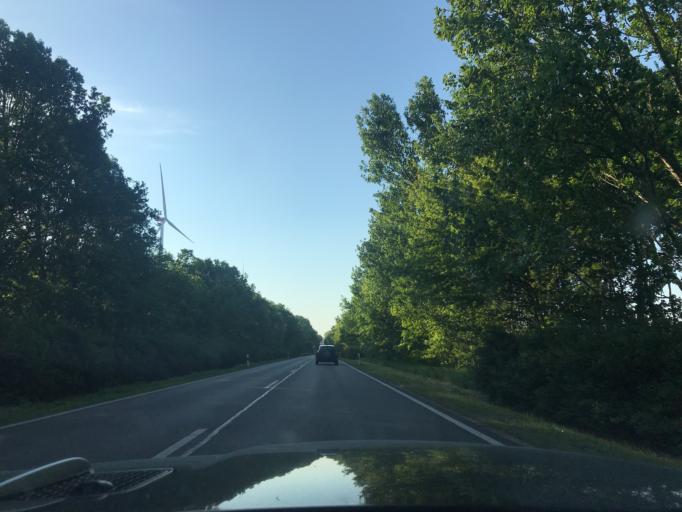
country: DE
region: Thuringia
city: Westhausen
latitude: 51.0246
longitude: 10.6786
